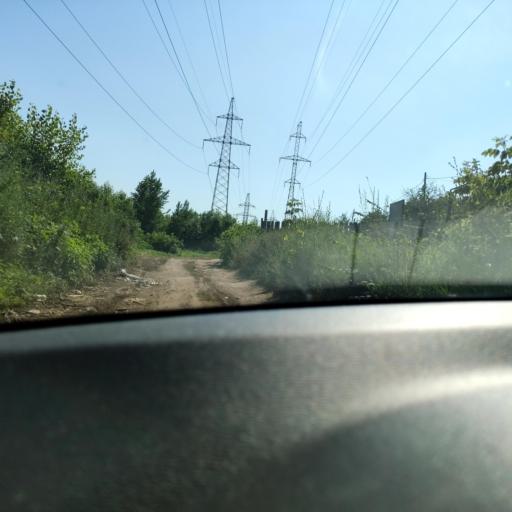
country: RU
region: Samara
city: Samara
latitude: 53.1767
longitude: 50.2159
